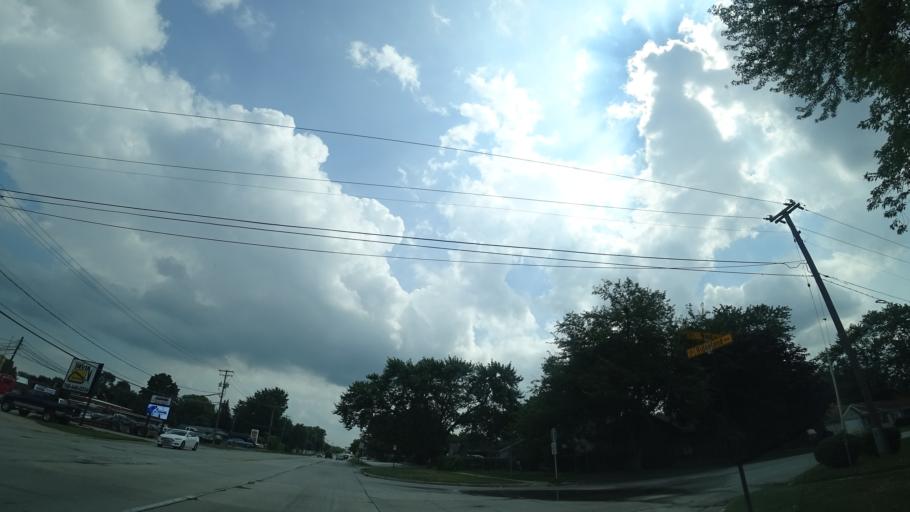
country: US
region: Illinois
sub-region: Cook County
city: Chicago Ridge
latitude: 41.6805
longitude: -87.7785
